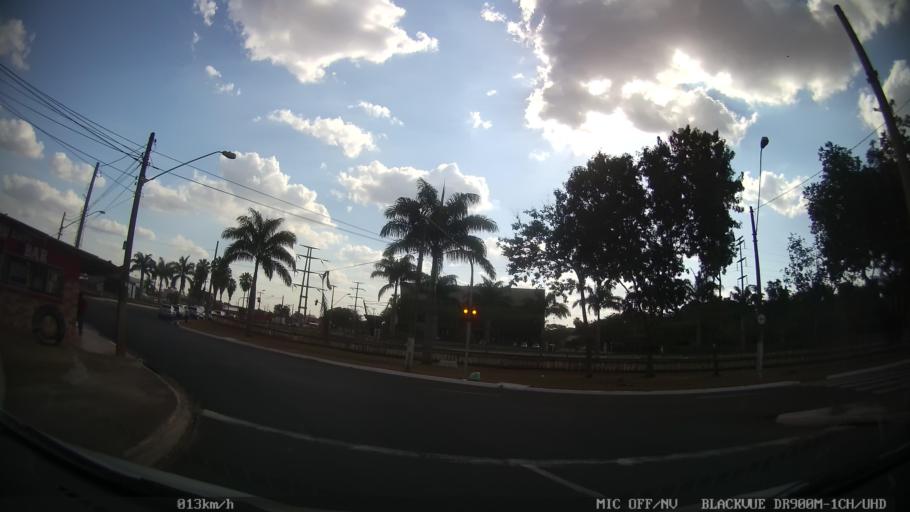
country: BR
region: Sao Paulo
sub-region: Ribeirao Preto
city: Ribeirao Preto
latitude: -21.1782
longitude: -47.8163
